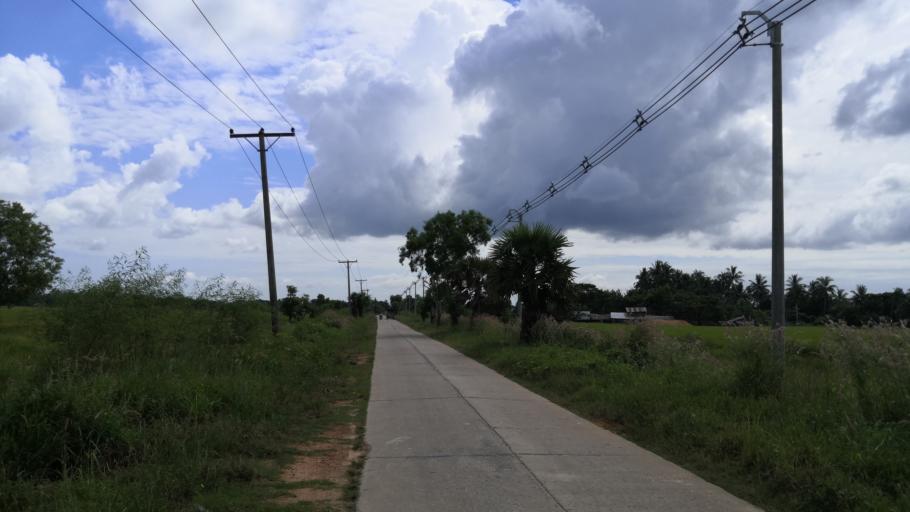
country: MM
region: Yangon
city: Kanbe
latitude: 16.4384
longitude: 96.1574
